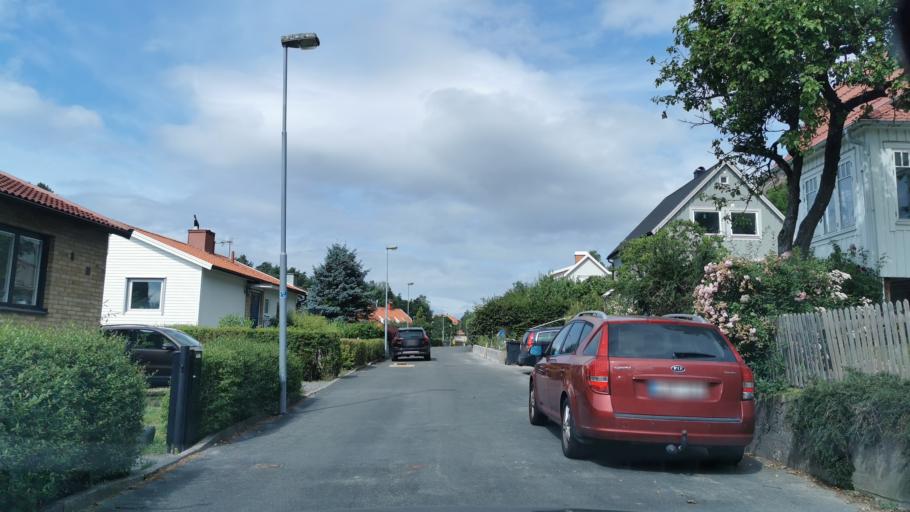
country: SE
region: Vaestra Goetaland
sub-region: Molndal
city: Moelndal
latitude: 57.6677
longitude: 11.9905
